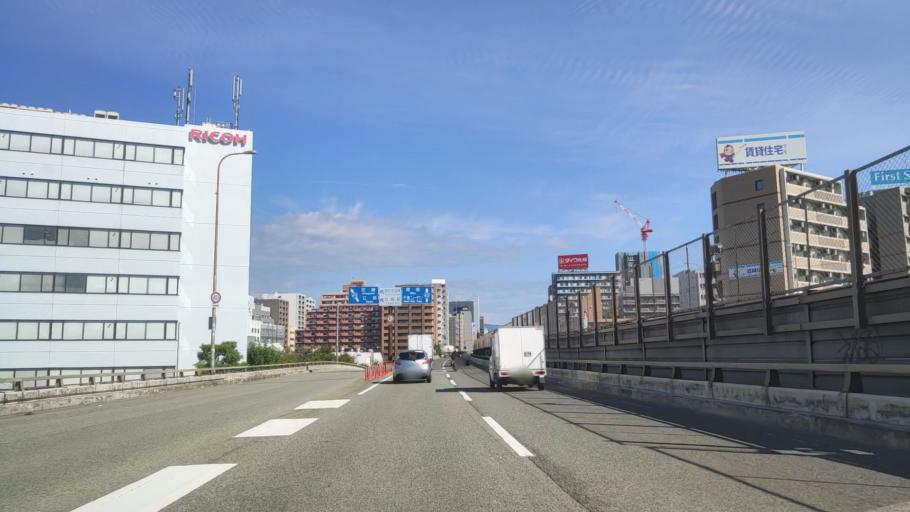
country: JP
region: Osaka
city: Suita
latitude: 34.7519
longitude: 135.4966
